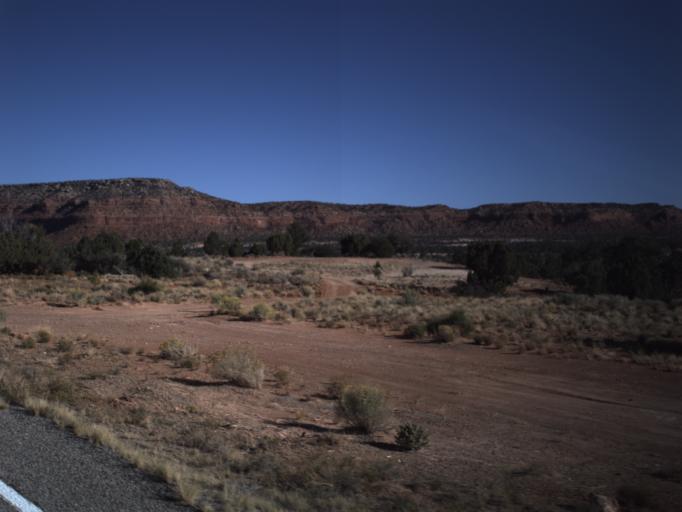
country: US
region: Utah
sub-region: San Juan County
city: Blanding
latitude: 37.6452
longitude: -110.1132
